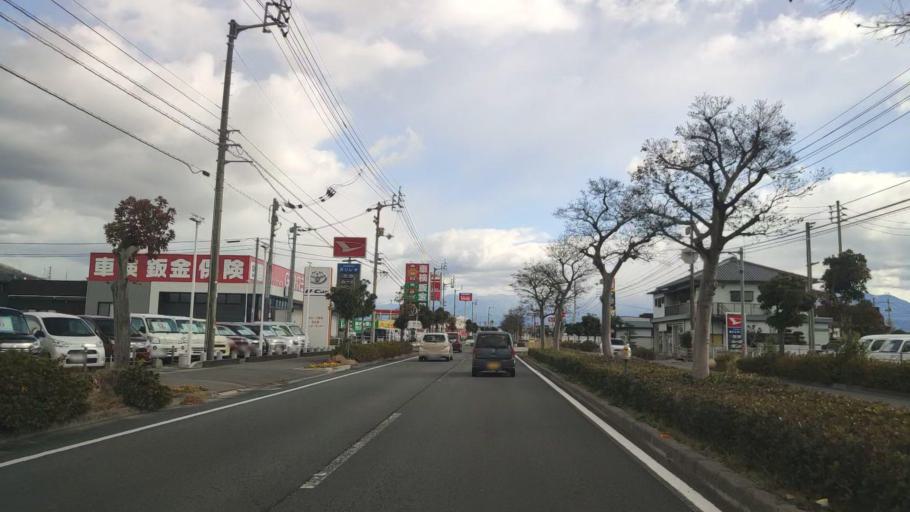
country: JP
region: Ehime
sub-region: Shikoku-chuo Shi
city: Matsuyama
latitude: 33.8198
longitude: 132.7900
